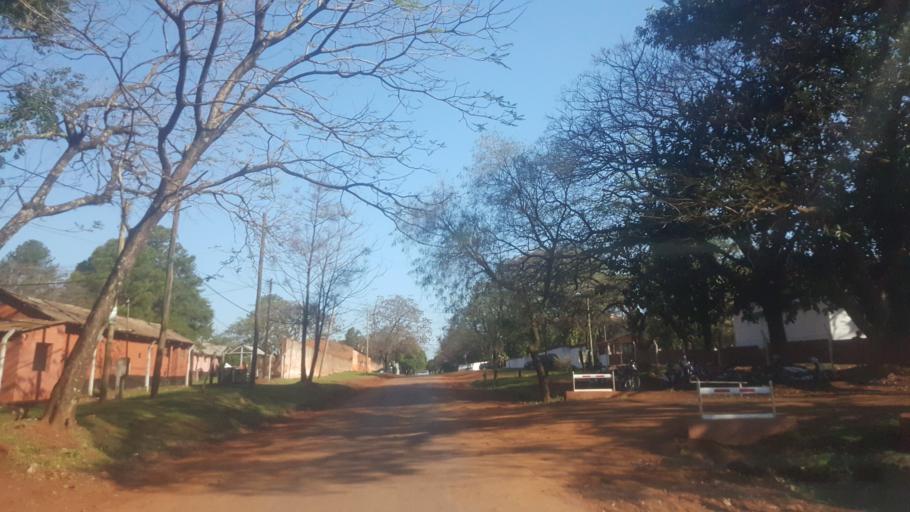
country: AR
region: Misiones
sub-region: Departamento de Capital
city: Posadas
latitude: -27.3634
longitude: -55.9198
